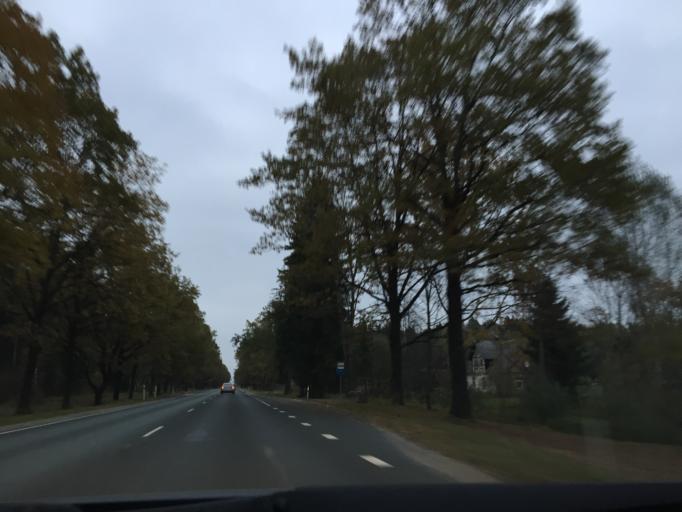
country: LV
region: Ozolnieku
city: Ozolnieki
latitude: 56.7031
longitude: 23.8156
